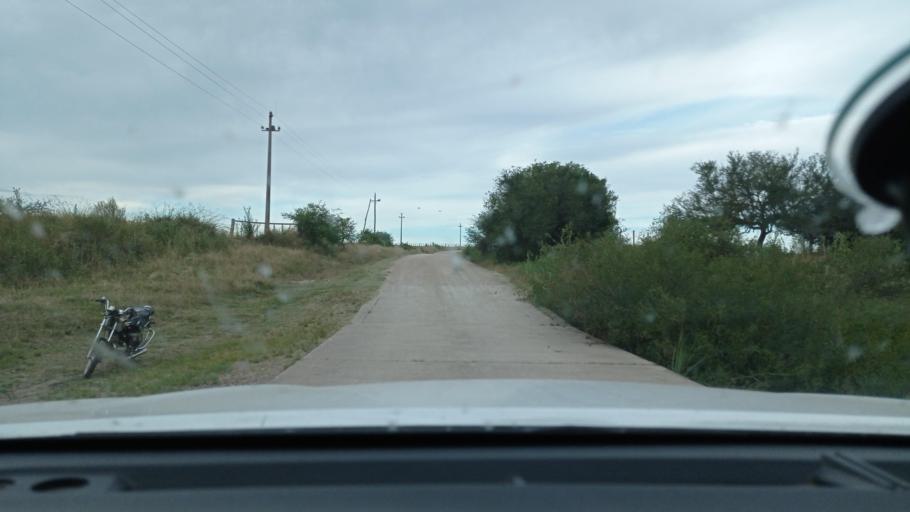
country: UY
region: Florida
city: Casupa
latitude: -34.1006
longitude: -55.7417
